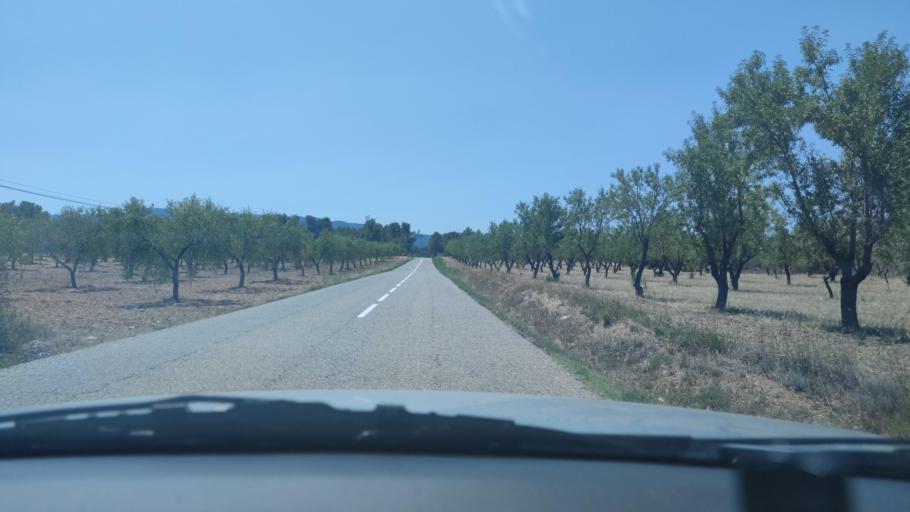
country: ES
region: Catalonia
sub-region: Provincia de Tarragona
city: Vallclara
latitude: 41.4028
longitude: 0.9564
